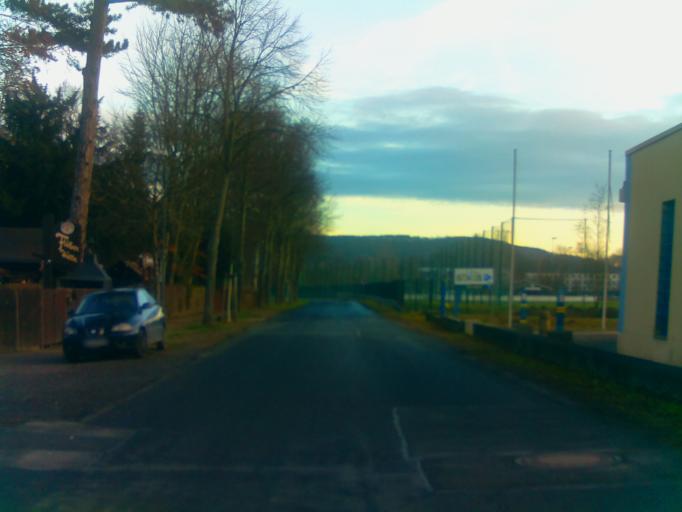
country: DE
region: Thuringia
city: Bad Blankenburg
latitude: 50.6741
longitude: 11.2690
